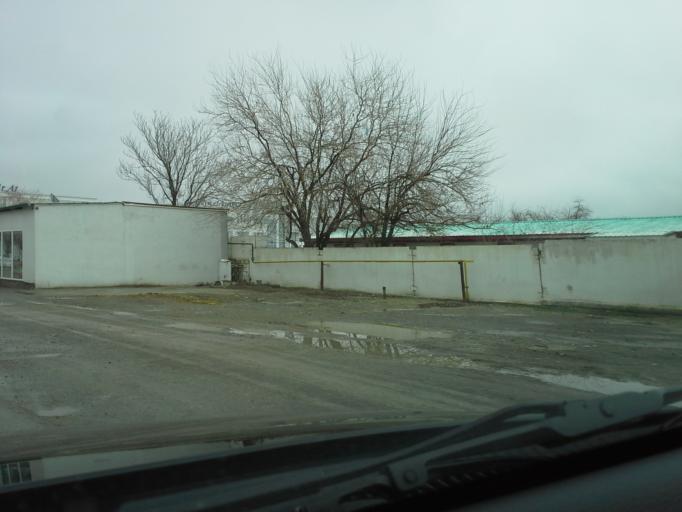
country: TM
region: Ahal
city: Ashgabat
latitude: 37.9522
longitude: 58.4251
